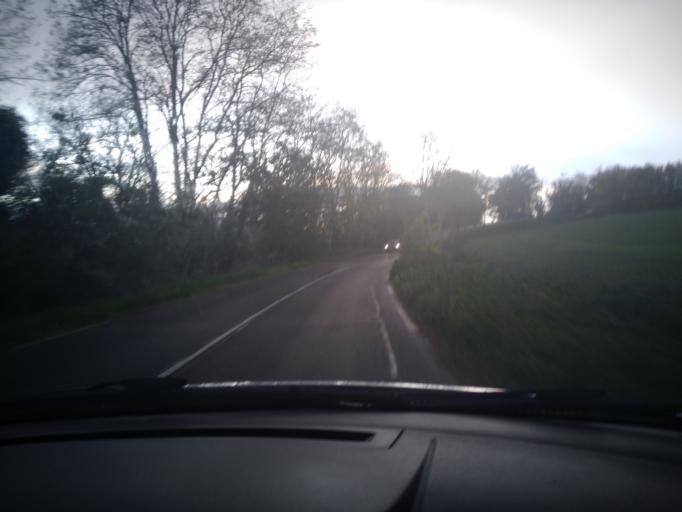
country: FR
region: Ile-de-France
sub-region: Departement des Yvelines
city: Feucherolles
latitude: 48.8552
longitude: 1.9707
